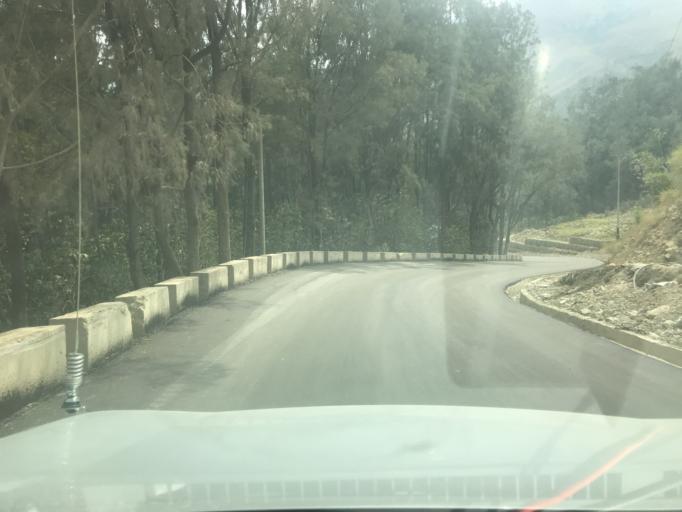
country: TL
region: Manufahi
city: Same
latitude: -8.8951
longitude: 125.5927
